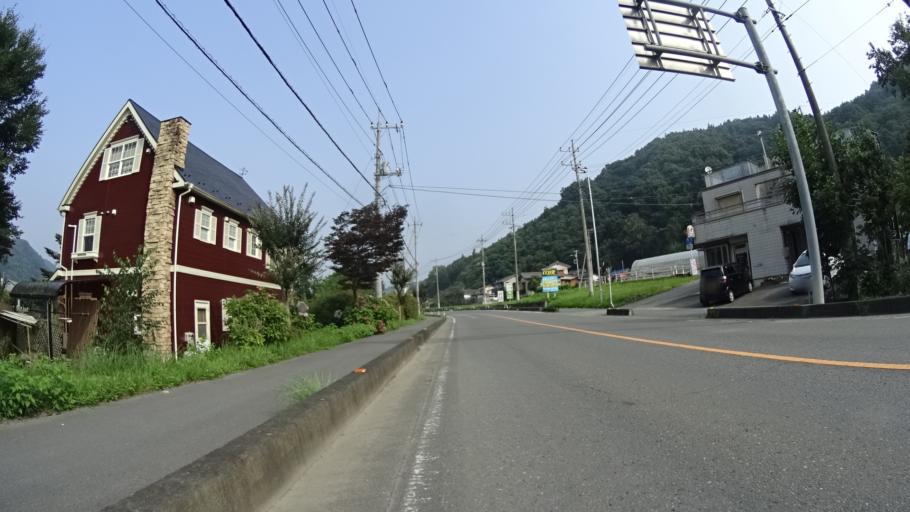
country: JP
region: Saitama
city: Chichibu
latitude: 36.0143
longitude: 139.0205
